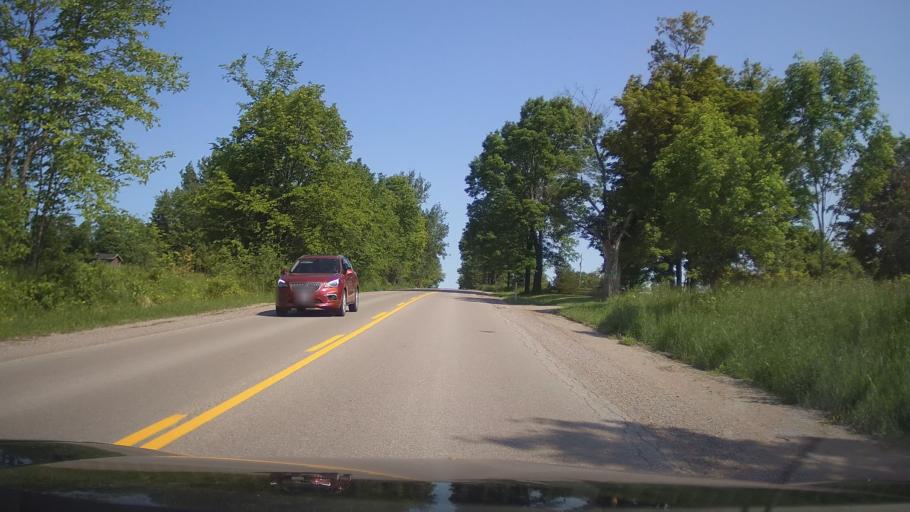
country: CA
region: Ontario
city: Uxbridge
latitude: 44.5270
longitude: -78.9634
